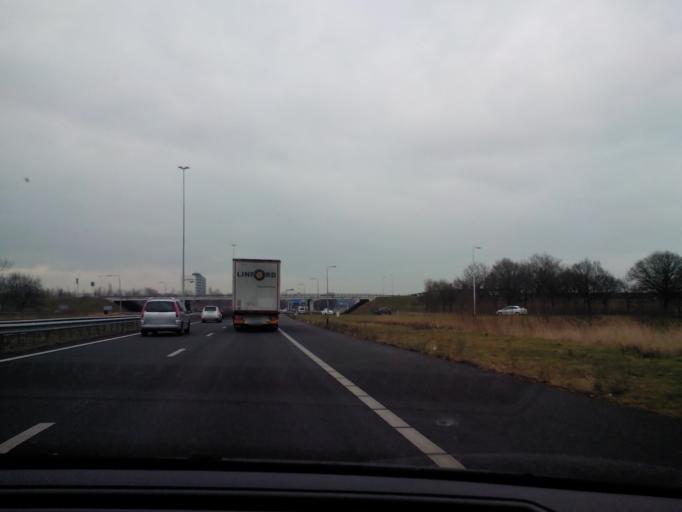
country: NL
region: North Brabant
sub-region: Gemeente Breda
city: Hoge Vucht
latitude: 51.5803
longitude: 4.8239
